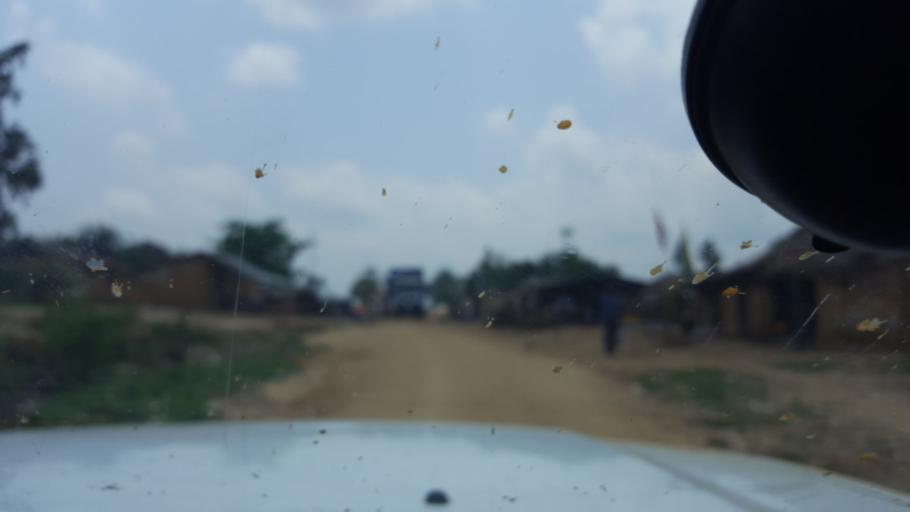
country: CD
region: Bandundu
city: Mushie
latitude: -3.7431
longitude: 16.6518
